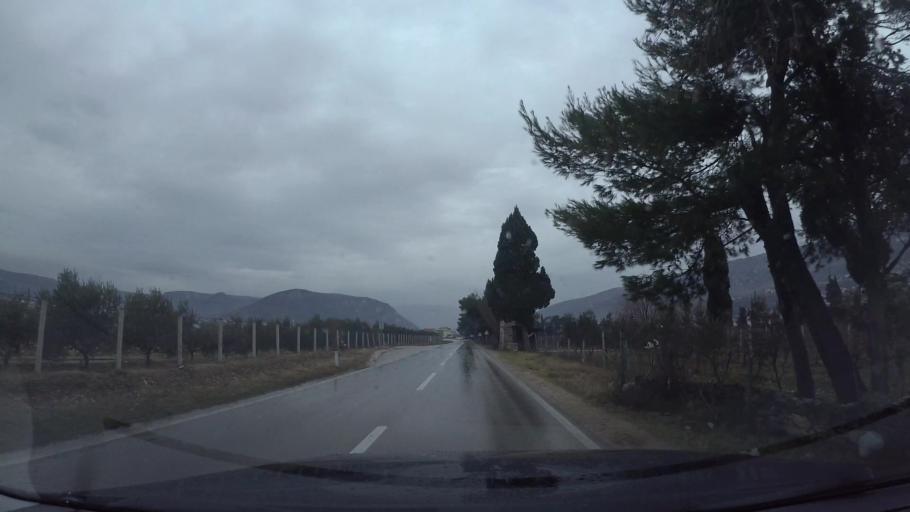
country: BA
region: Federation of Bosnia and Herzegovina
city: Rodoc
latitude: 43.2993
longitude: 17.8416
